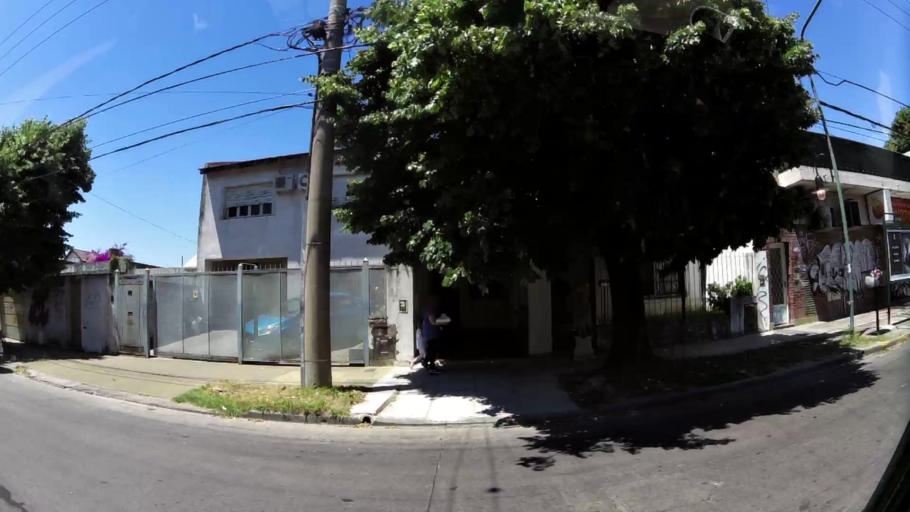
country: AR
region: Buenos Aires
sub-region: Partido de Vicente Lopez
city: Olivos
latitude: -34.5024
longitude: -58.5079
